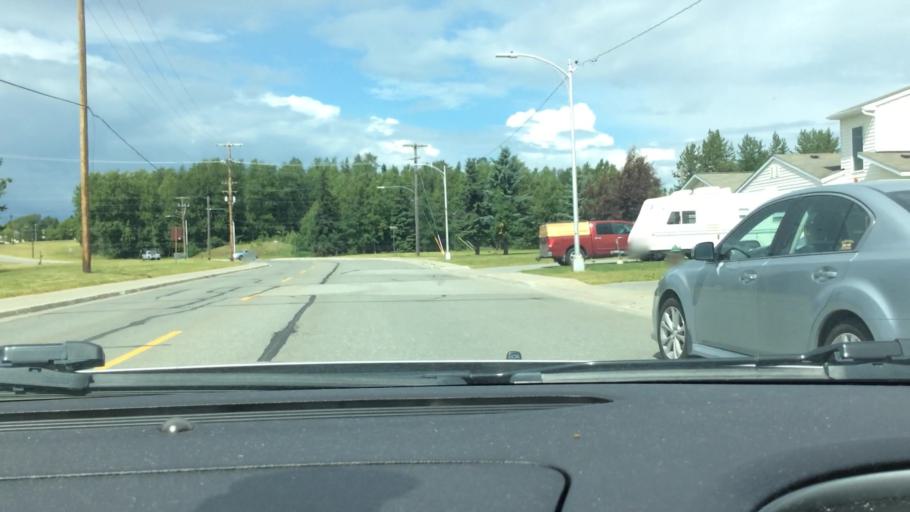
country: US
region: Alaska
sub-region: Anchorage Municipality
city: Anchorage
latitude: 61.2353
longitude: -149.8687
